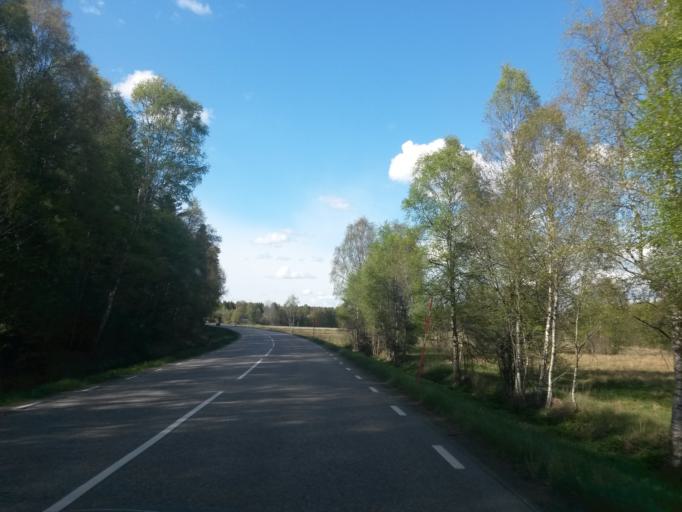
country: SE
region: Vaestra Goetaland
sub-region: Herrljunga Kommun
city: Herrljunga
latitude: 57.9358
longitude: 13.0256
